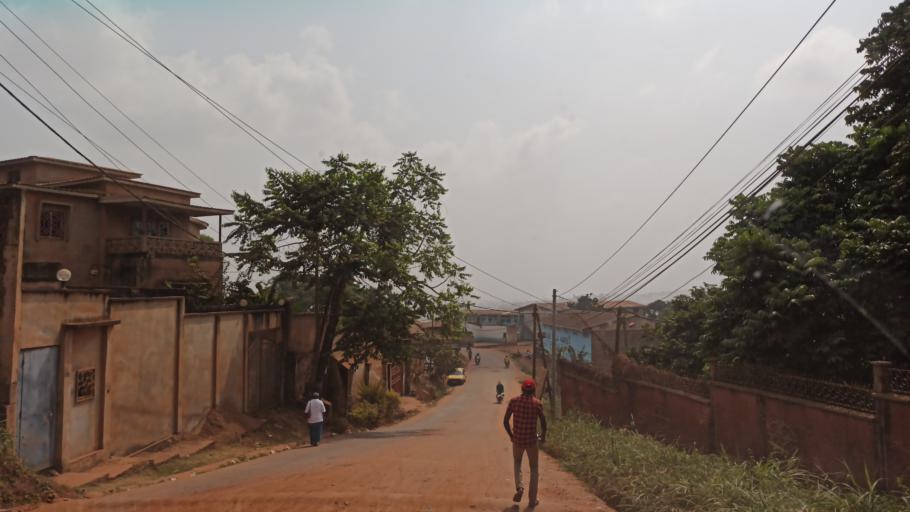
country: CM
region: Centre
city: Yaounde
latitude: 3.8770
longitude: 11.4818
